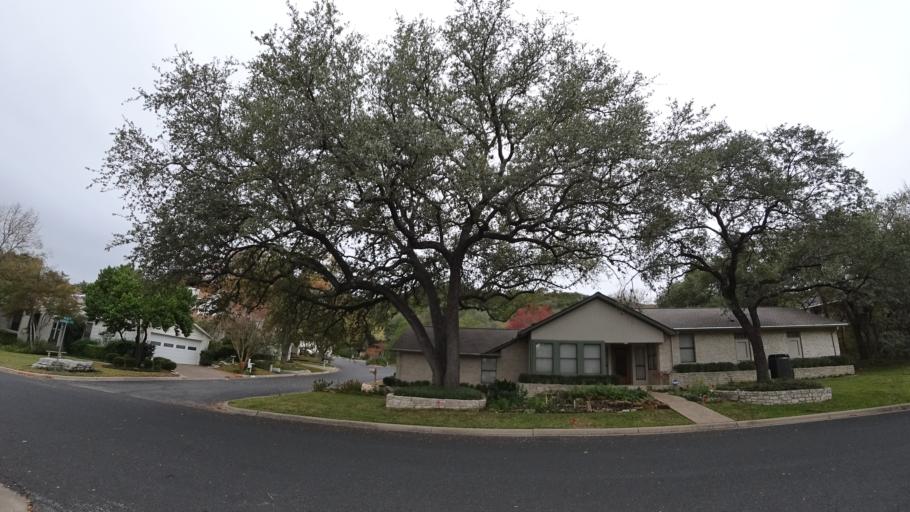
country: US
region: Texas
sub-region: Williamson County
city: Jollyville
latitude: 30.3718
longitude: -97.7897
